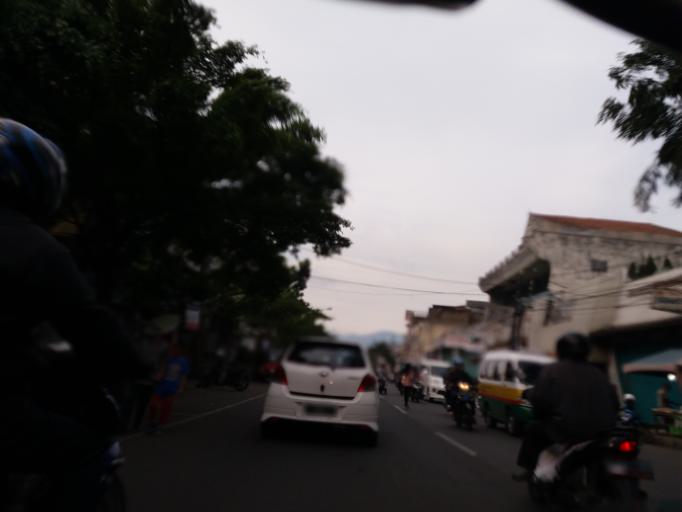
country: ID
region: West Java
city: Bandung
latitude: -6.9059
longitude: 107.6486
